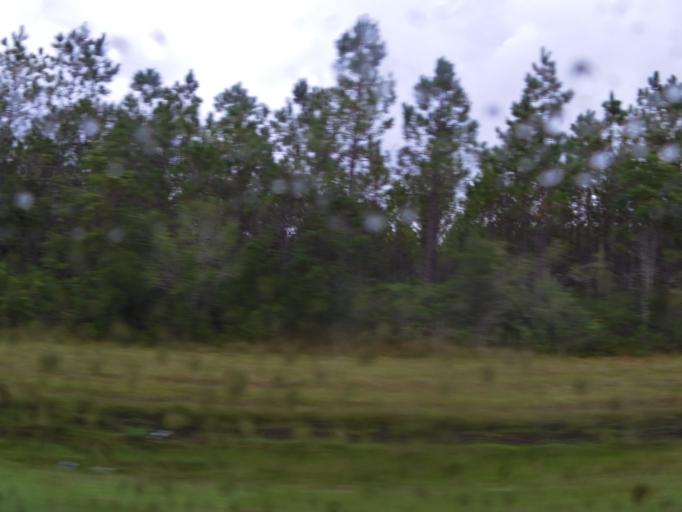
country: US
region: Florida
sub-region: Nassau County
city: Callahan
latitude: 30.4957
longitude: -81.9967
